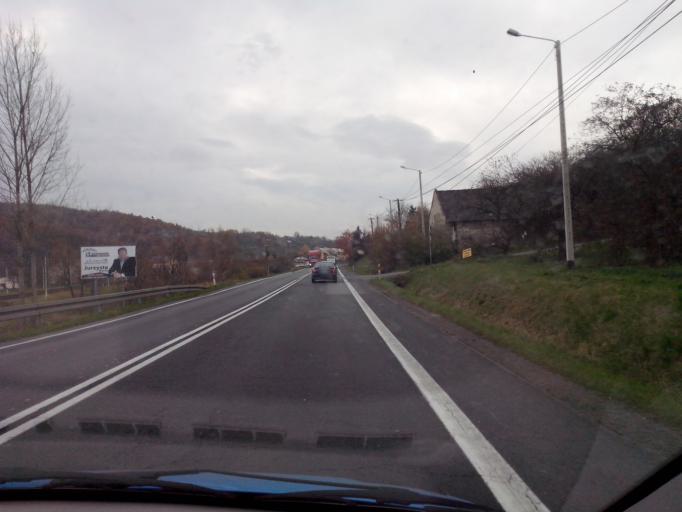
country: PL
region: Subcarpathian Voivodeship
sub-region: Powiat rzeszowski
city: Lubenia
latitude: 49.9363
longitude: 21.9033
